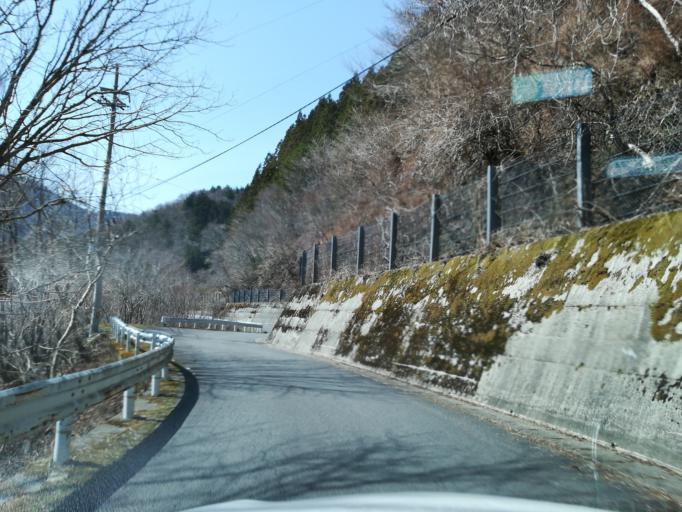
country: JP
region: Tokushima
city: Wakimachi
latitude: 33.8525
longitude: 134.0375
